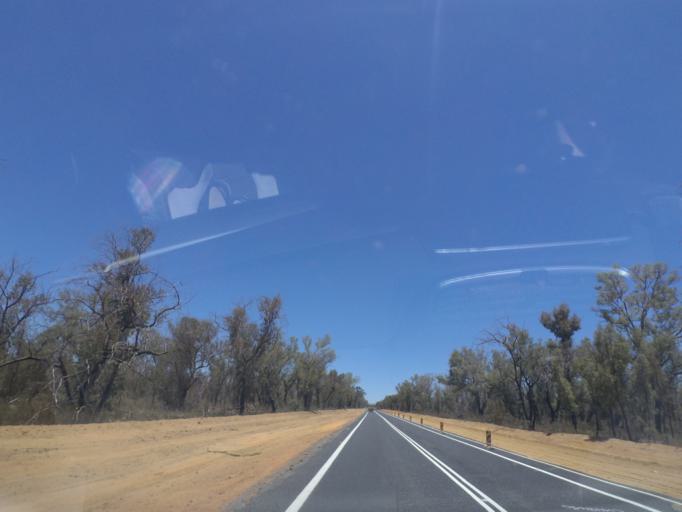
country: AU
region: New South Wales
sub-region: Warrumbungle Shire
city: Coonabarabran
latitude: -30.9333
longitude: 149.4275
